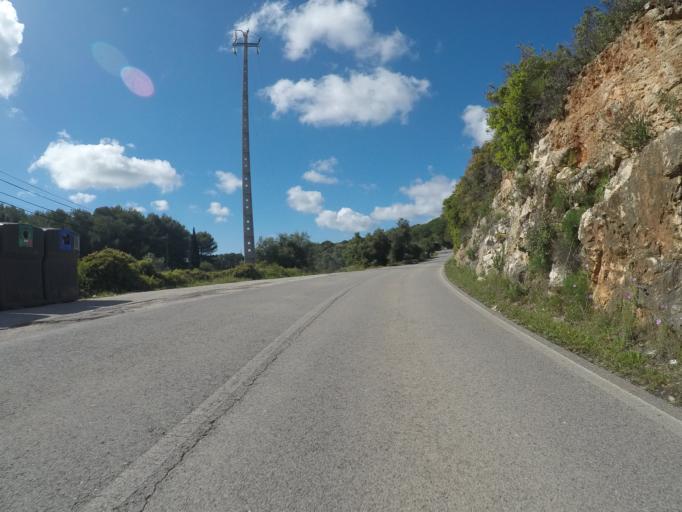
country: PT
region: Faro
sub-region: Vila do Bispo
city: Vila do Bispo
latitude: 37.0755
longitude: -8.8314
